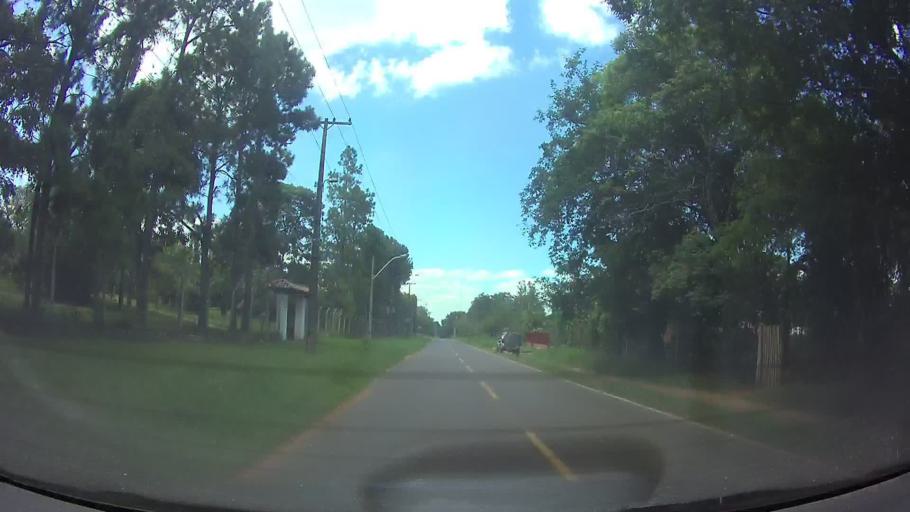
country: PY
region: Central
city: Itaugua
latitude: -25.3651
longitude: -57.3464
